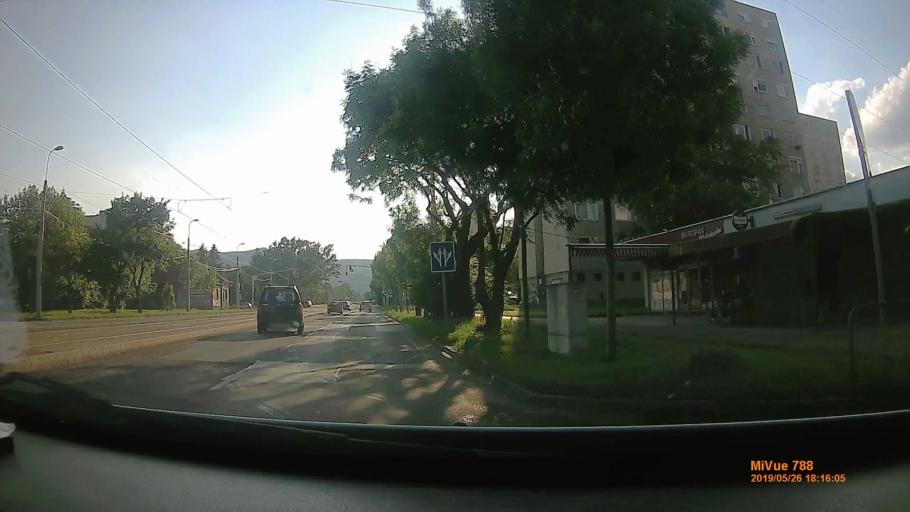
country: HU
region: Borsod-Abauj-Zemplen
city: Sajobabony
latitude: 48.1004
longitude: 20.7120
